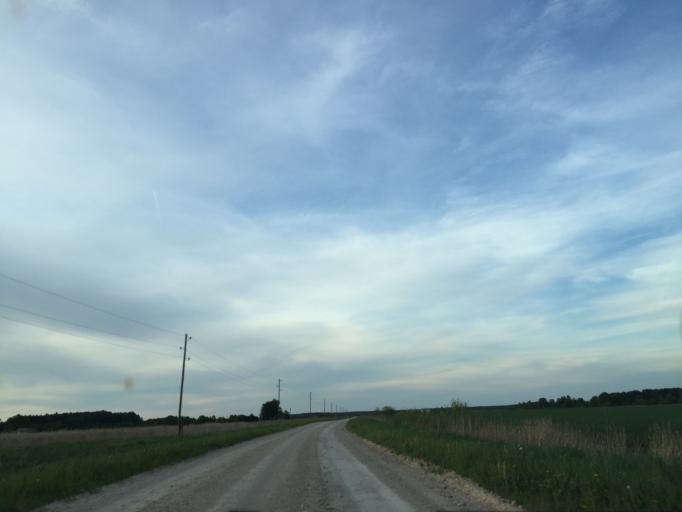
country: LV
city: Tireli
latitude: 56.7943
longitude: 23.5655
